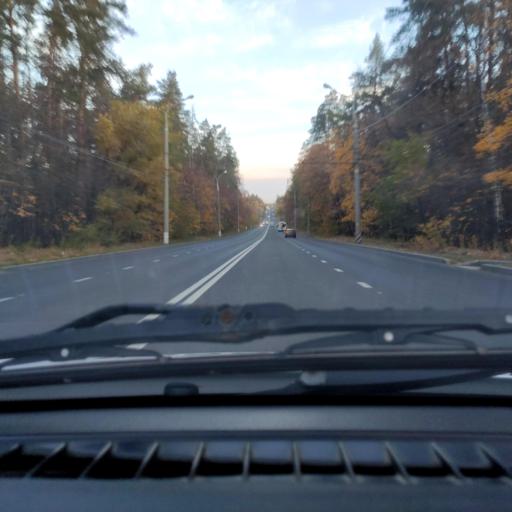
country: RU
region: Samara
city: Zhigulevsk
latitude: 53.4956
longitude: 49.4631
